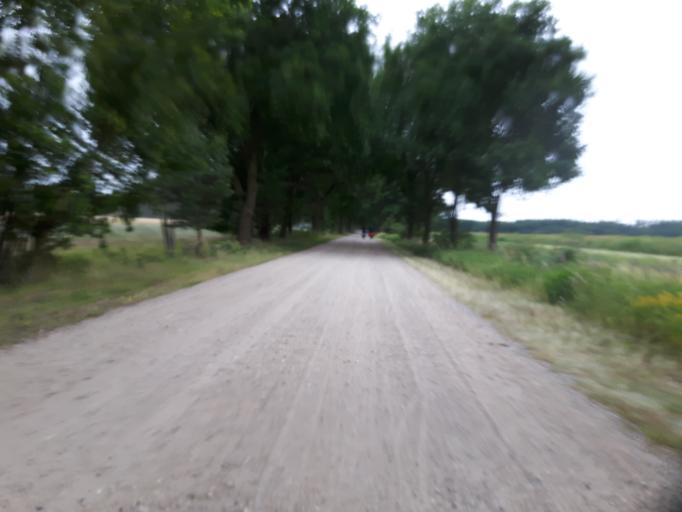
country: DE
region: Lower Saxony
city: Winsen
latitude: 53.3226
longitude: 10.1980
